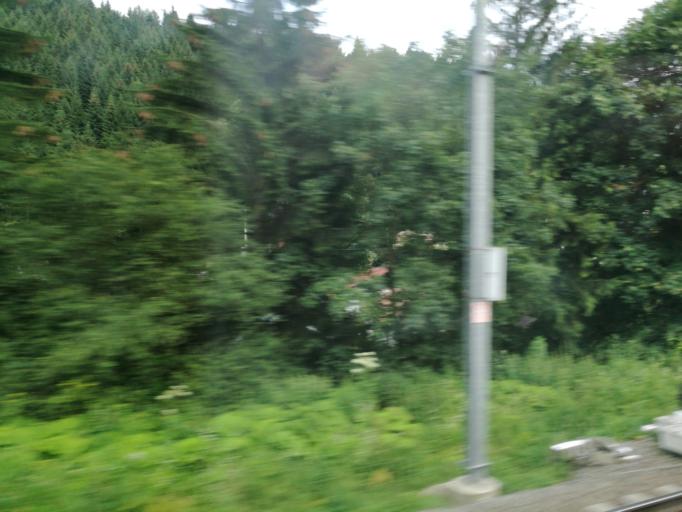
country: RO
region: Prahova
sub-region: Oras Azuga
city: Azuga
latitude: 45.4408
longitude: 25.5508
